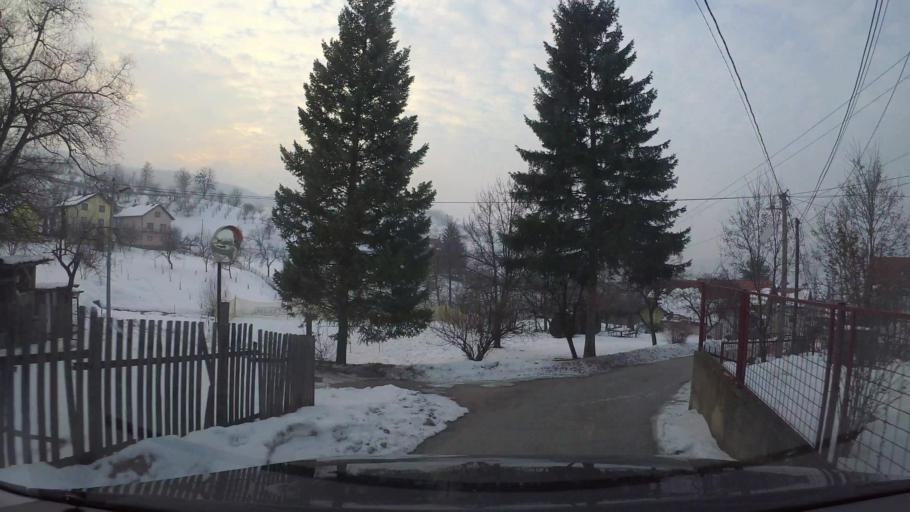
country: BA
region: Federation of Bosnia and Herzegovina
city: Hotonj
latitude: 43.8910
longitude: 18.3643
